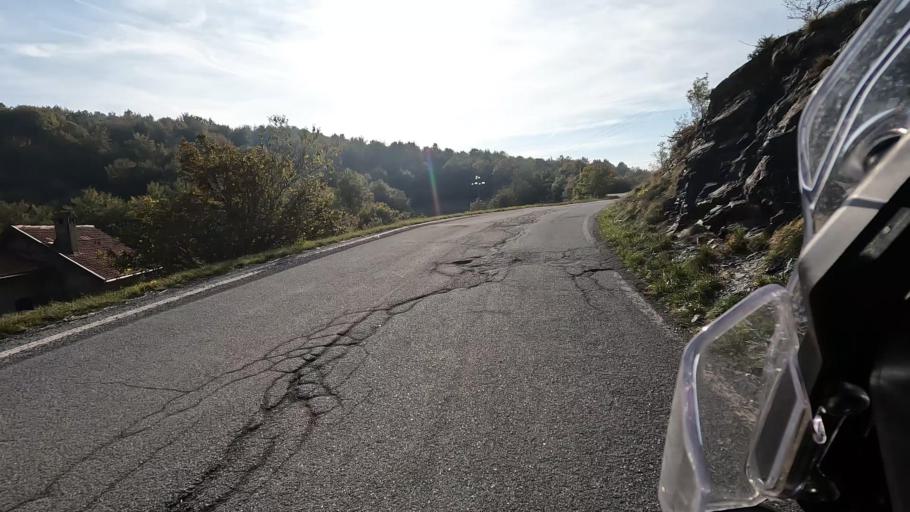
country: IT
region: Liguria
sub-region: Provincia di Savona
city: Urbe
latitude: 44.4765
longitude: 8.5650
